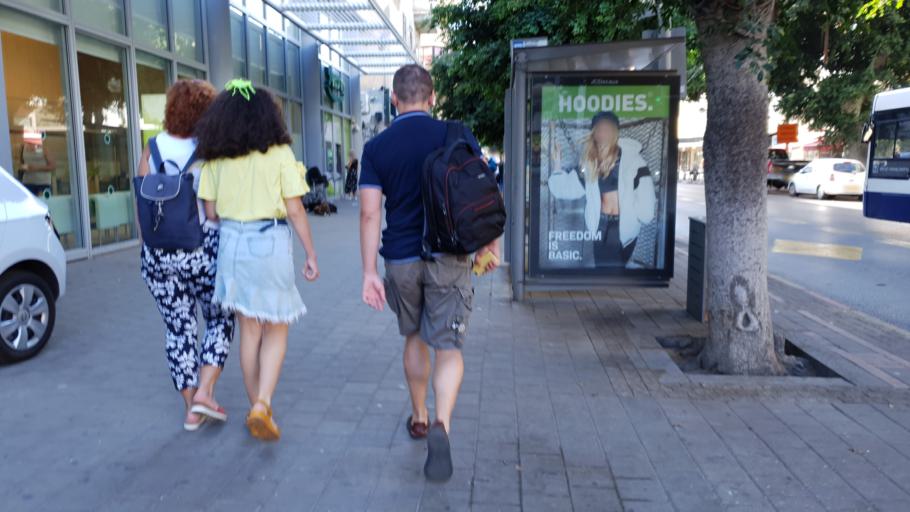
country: IL
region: Tel Aviv
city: Tel Aviv
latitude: 32.0796
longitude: 34.7740
